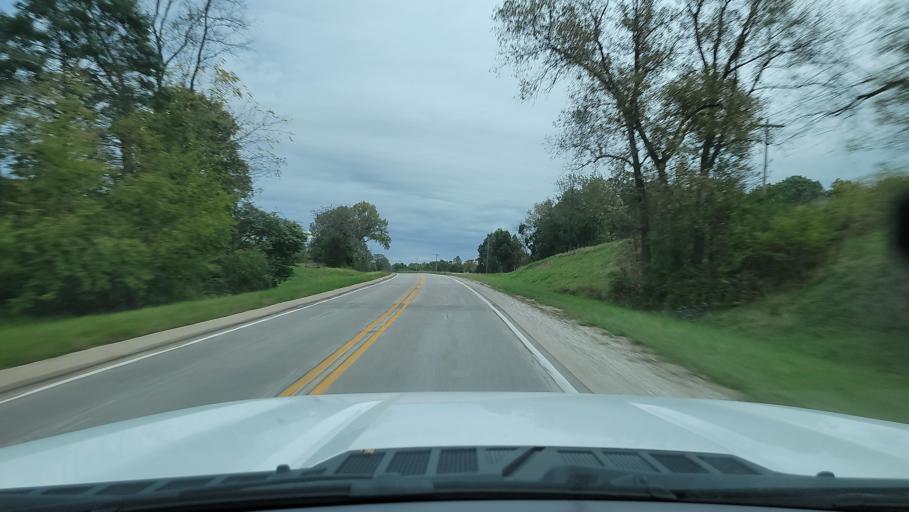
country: US
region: Illinois
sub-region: Schuyler County
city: Rushville
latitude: 40.0397
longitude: -90.6162
